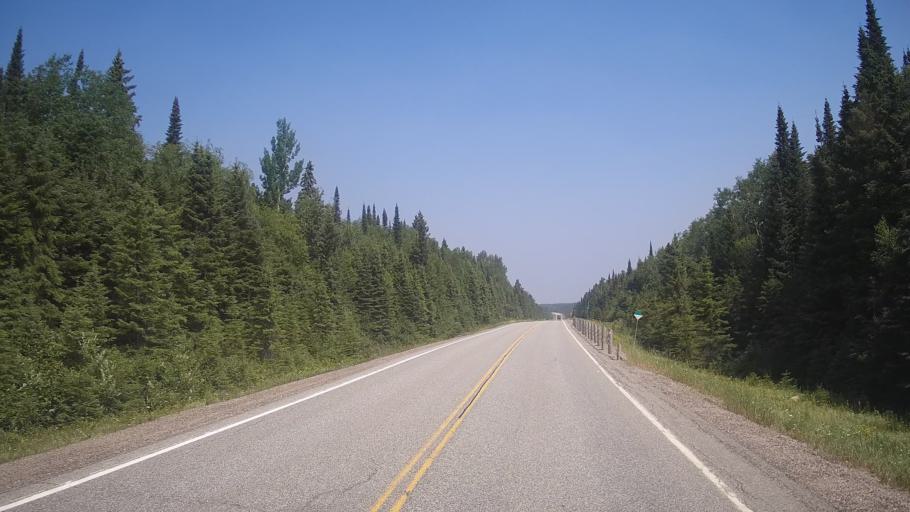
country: CA
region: Ontario
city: Timmins
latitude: 48.0849
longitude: -81.5963
